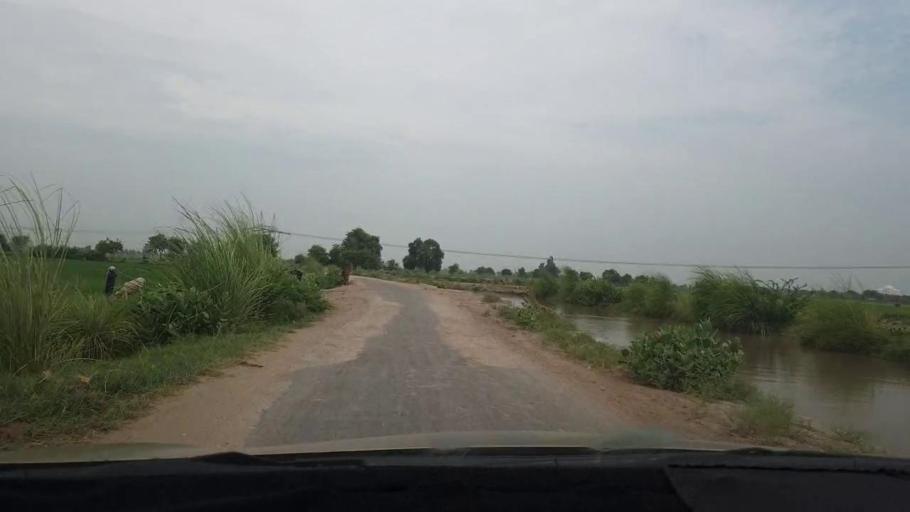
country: PK
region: Sindh
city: Naudero
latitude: 27.6785
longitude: 68.3413
